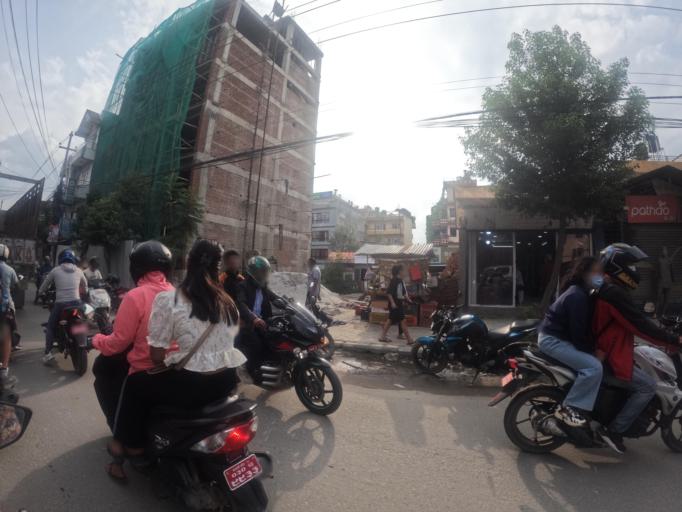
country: NP
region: Central Region
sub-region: Bagmati Zone
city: Bhaktapur
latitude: 27.6759
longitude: 85.3978
